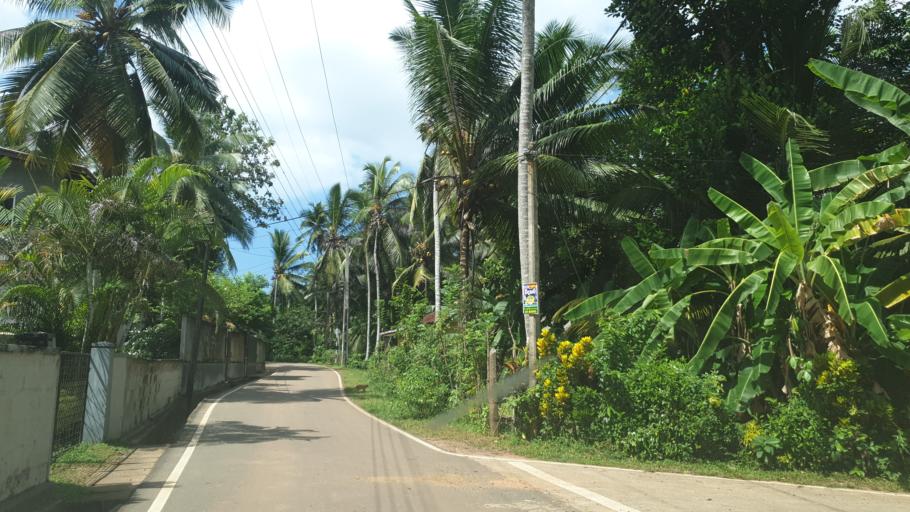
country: LK
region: Western
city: Panadura
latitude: 6.6757
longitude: 79.9650
